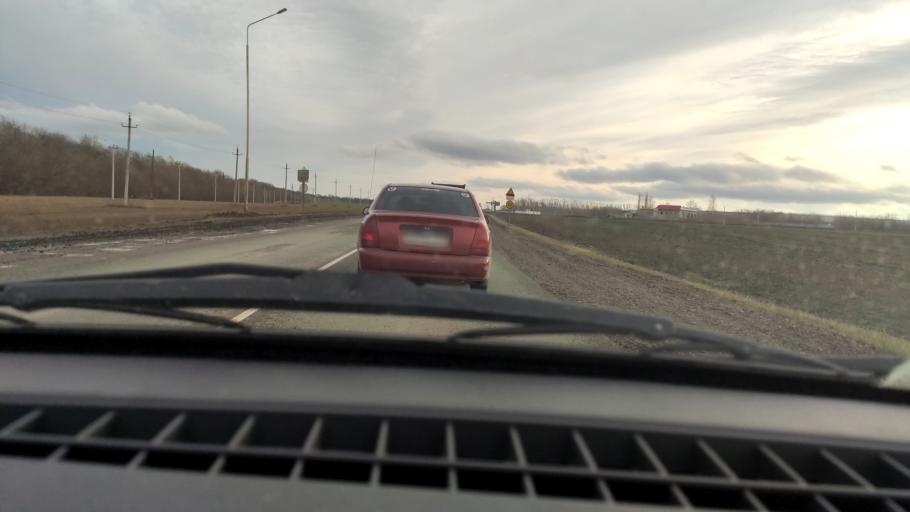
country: RU
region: Bashkortostan
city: Chishmy
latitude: 54.5712
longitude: 55.3547
